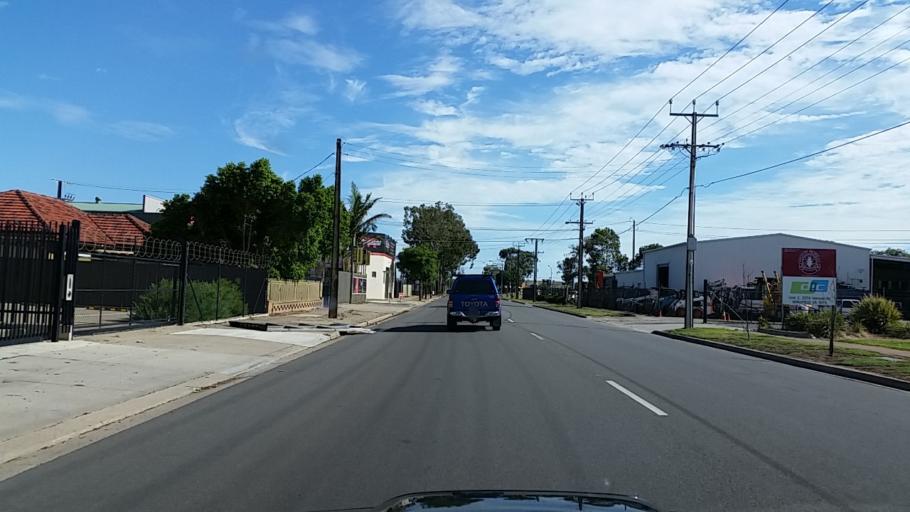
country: AU
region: South Australia
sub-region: Charles Sturt
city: Woodville North
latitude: -34.8479
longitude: 138.5466
